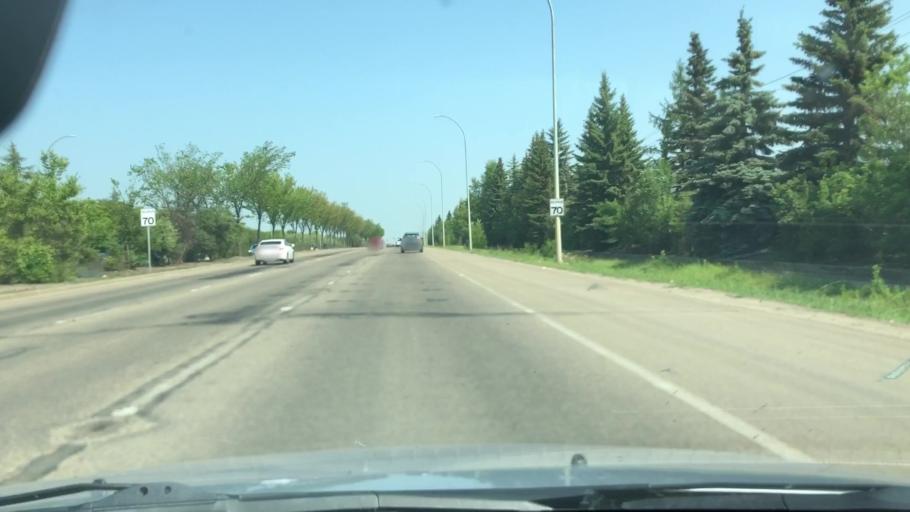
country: CA
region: Alberta
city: Edmonton
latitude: 53.6084
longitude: -113.4917
